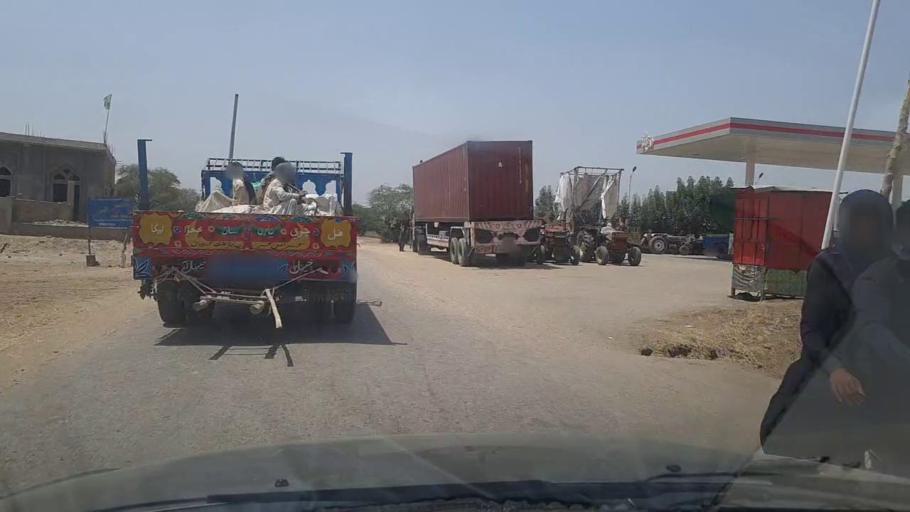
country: PK
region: Sindh
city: Pad Idan
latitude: 26.8823
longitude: 68.2997
